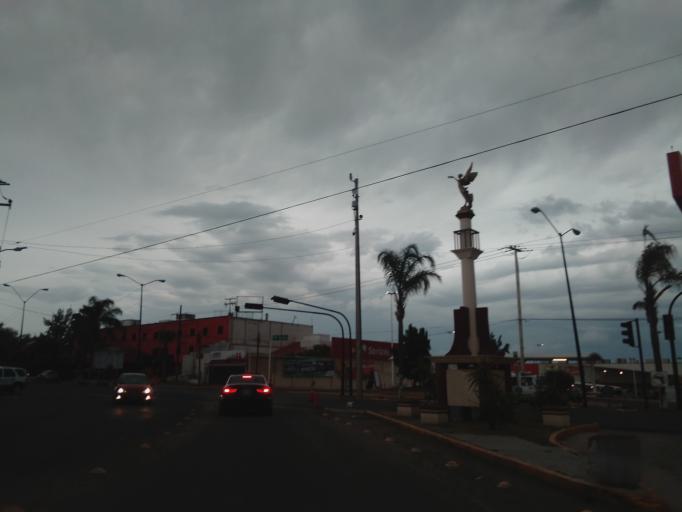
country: MX
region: Guanajuato
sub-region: Dolores Hidalgo Cuna de la Independencia Nacional
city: Dolores Hidalgo Cuna de la Independencia Nacional
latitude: 21.1566
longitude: -100.9217
